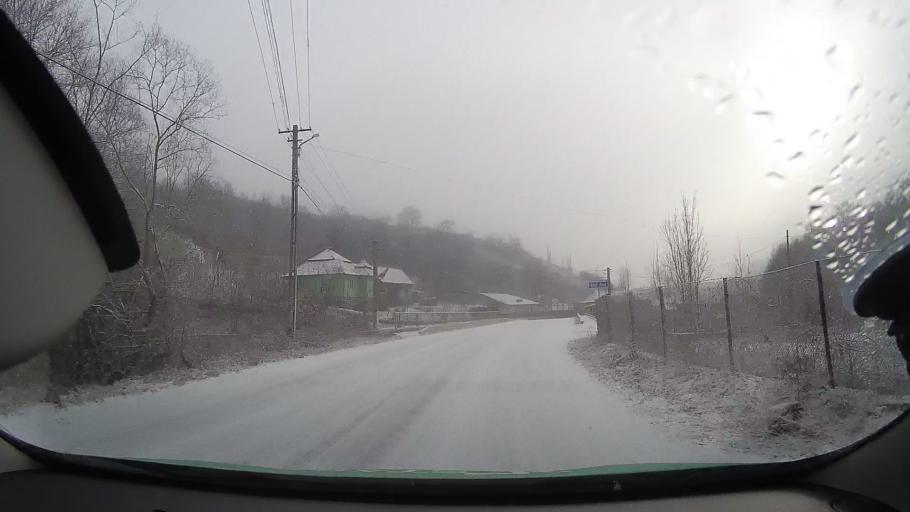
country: RO
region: Alba
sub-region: Comuna Livezile
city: Livezile
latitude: 46.3657
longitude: 23.6071
